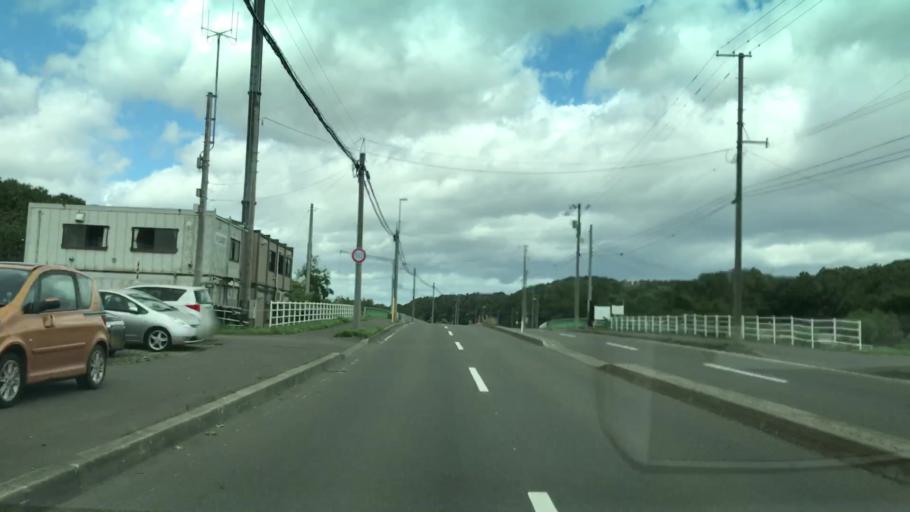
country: JP
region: Hokkaido
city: Kitahiroshima
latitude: 42.9730
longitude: 141.4505
